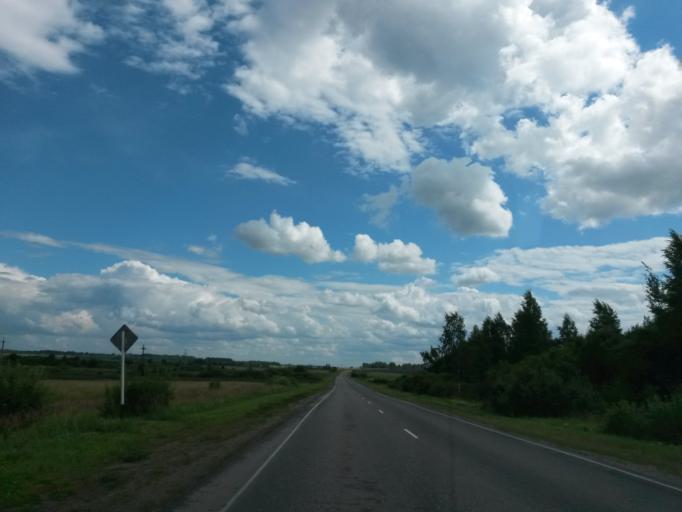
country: RU
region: Jaroslavl
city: Dubki
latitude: 57.1990
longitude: 40.3400
